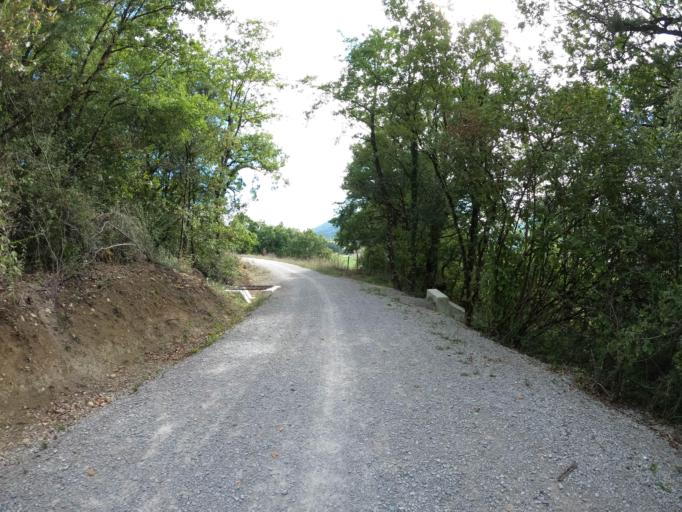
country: ES
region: Navarre
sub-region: Provincia de Navarra
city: Irurtzun
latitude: 42.9239
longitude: -1.8289
